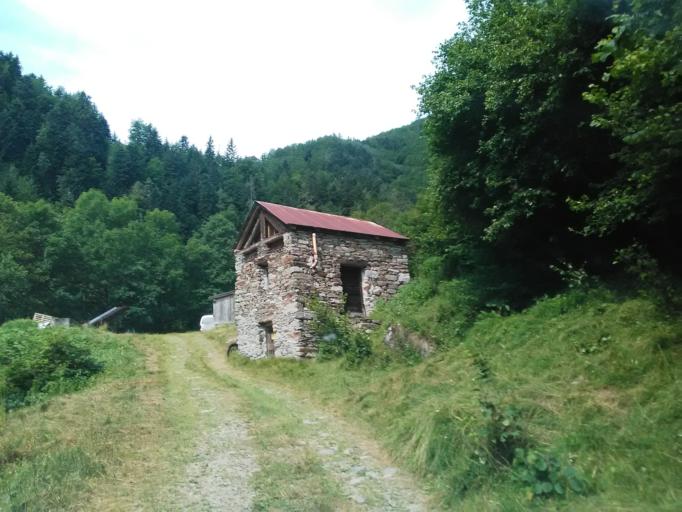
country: IT
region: Piedmont
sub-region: Provincia di Vercelli
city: Cervatto
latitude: 45.8785
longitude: 8.1542
